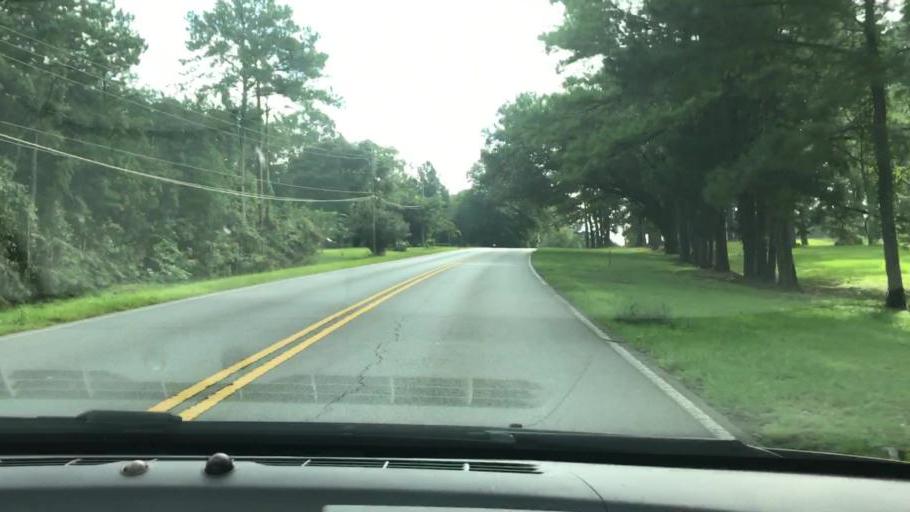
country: US
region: Florida
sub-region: Jackson County
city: Marianna
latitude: 30.7692
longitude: -85.2454
